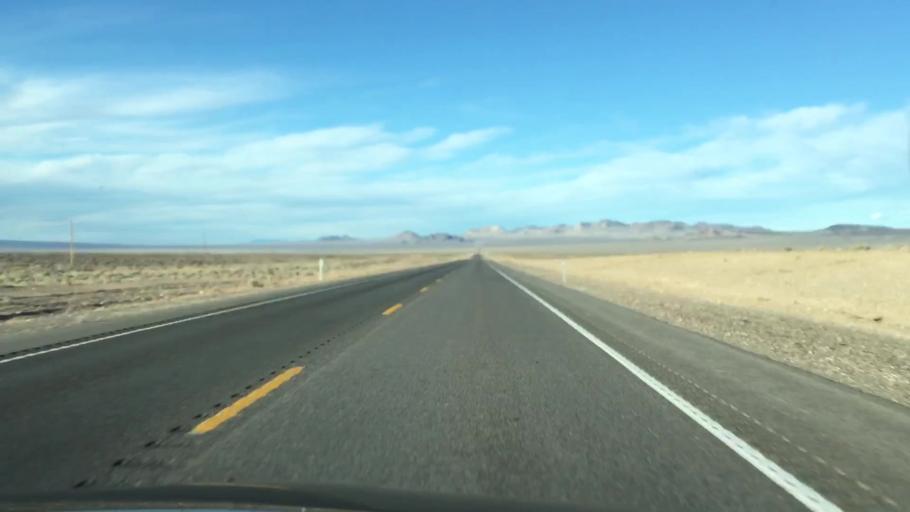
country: US
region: Nevada
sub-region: Esmeralda County
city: Goldfield
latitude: 37.8070
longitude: -117.2396
